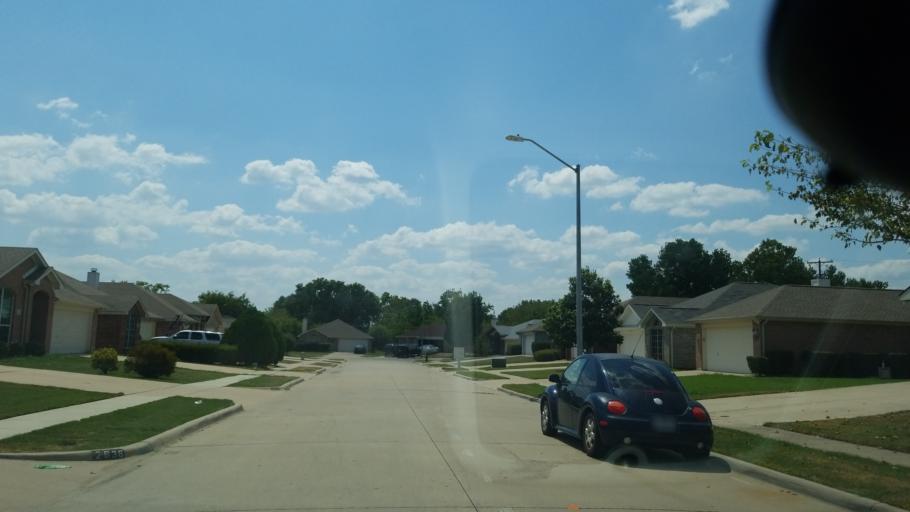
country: US
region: Texas
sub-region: Dallas County
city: Grand Prairie
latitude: 32.7074
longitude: -96.9915
